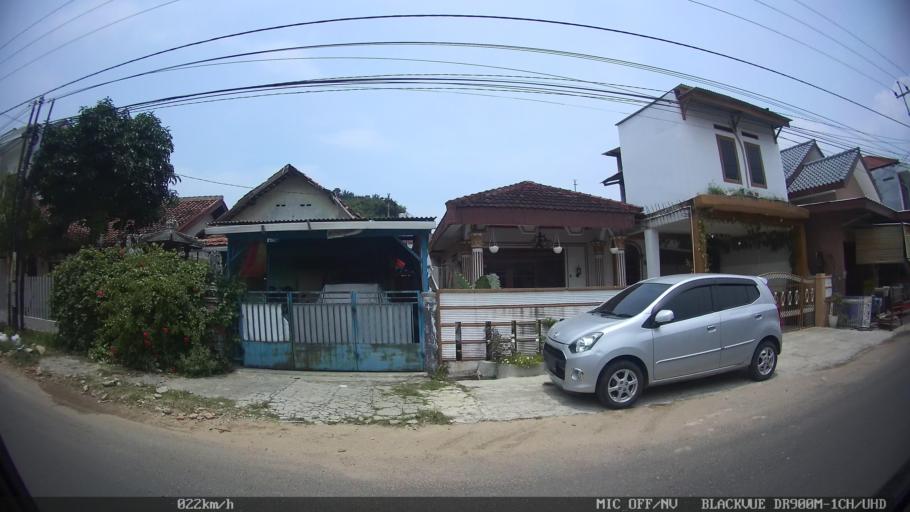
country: ID
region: Lampung
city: Bandarlampung
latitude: -5.4144
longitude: 105.2682
